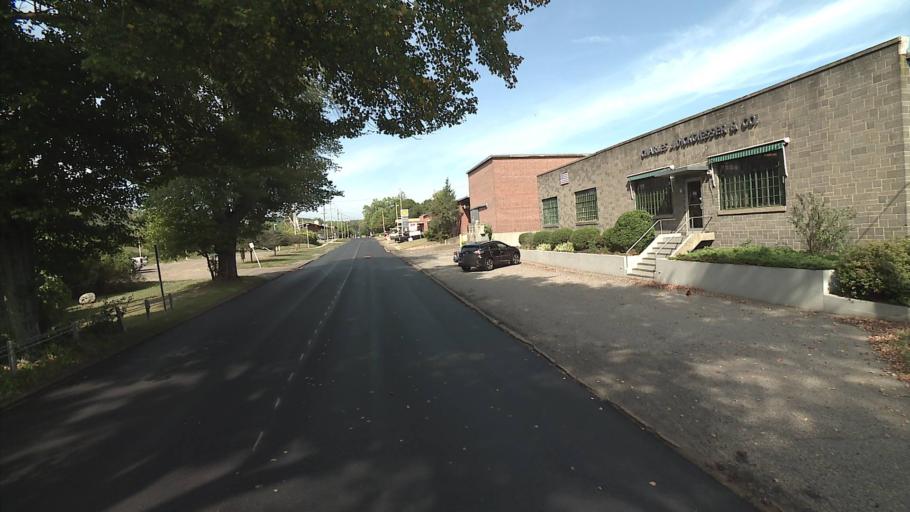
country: US
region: Connecticut
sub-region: Fairfield County
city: Shelton
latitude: 41.3268
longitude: -73.1012
